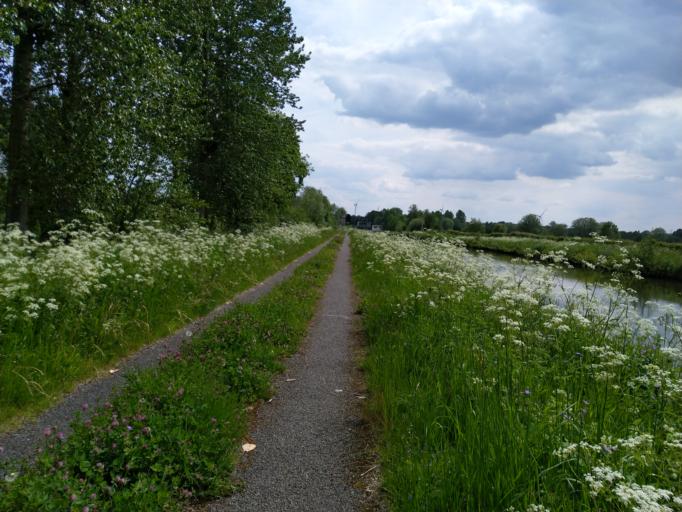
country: FR
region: Picardie
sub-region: Departement de l'Aisne
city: Wassigny
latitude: 50.0510
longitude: 3.6432
